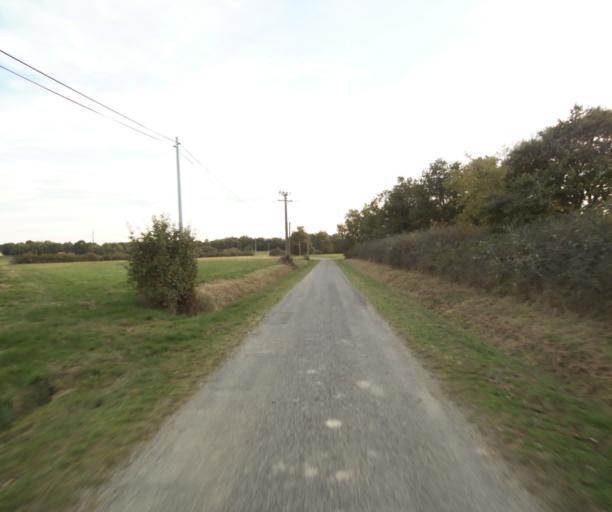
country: FR
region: Midi-Pyrenees
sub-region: Departement du Tarn-et-Garonne
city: Pompignan
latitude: 43.8218
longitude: 1.3230
